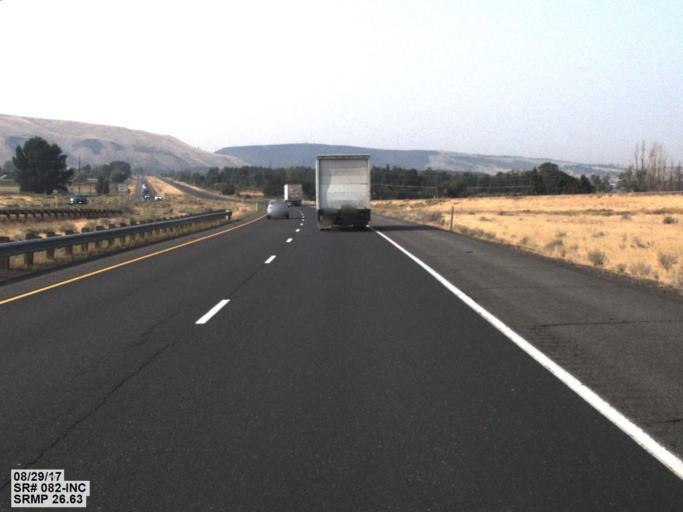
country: US
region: Washington
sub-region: Yakima County
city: Selah
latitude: 46.6776
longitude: -120.4816
